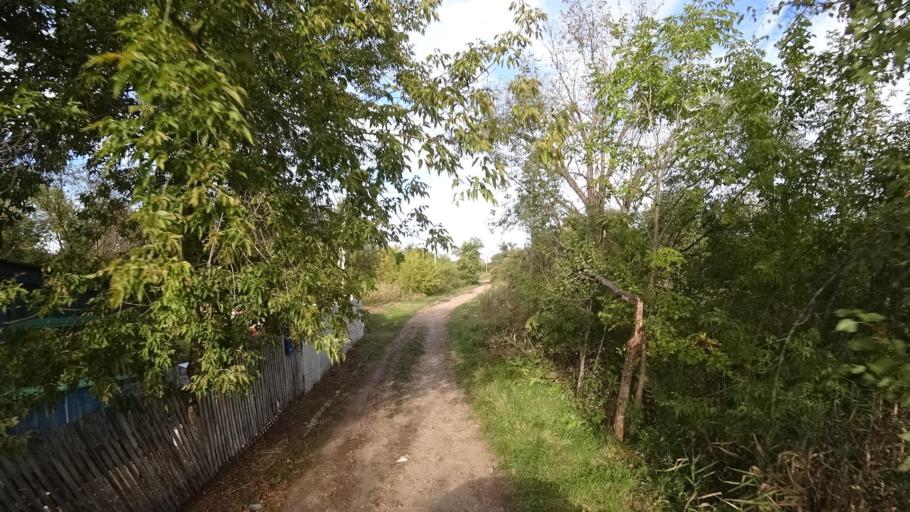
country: RU
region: Primorskiy
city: Dostoyevka
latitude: 44.2929
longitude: 133.4242
